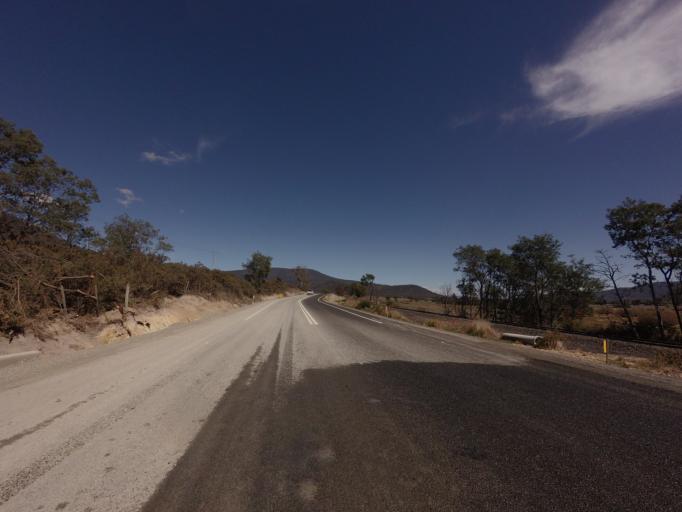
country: AU
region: Tasmania
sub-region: Break O'Day
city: St Helens
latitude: -41.6598
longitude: 147.9149
